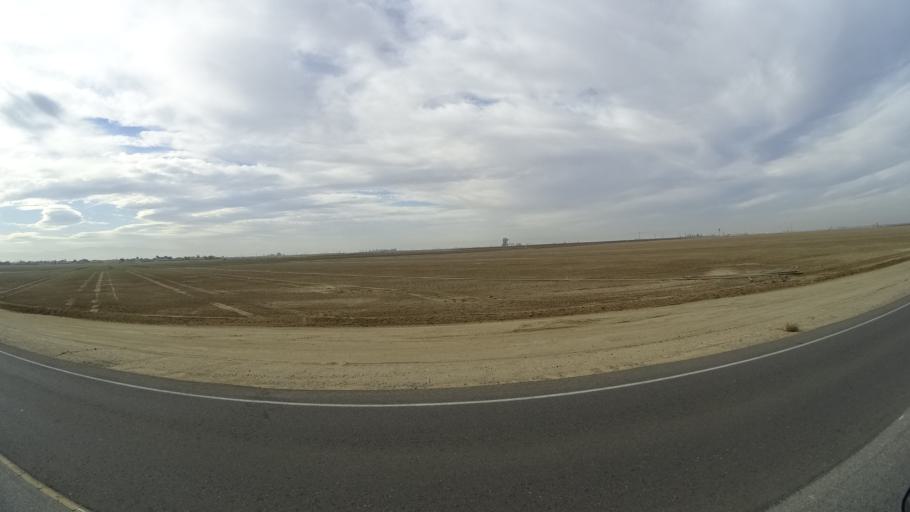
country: US
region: California
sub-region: Kern County
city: Rosedale
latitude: 35.4141
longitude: -119.1655
